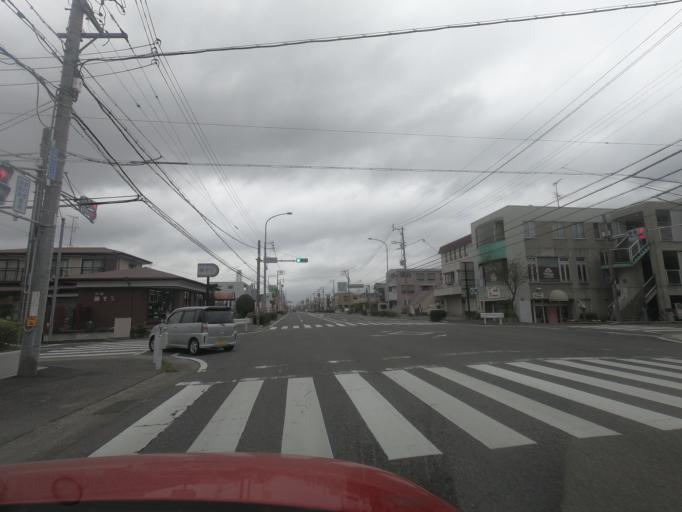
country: JP
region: Aichi
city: Kasugai
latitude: 35.2550
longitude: 136.9696
